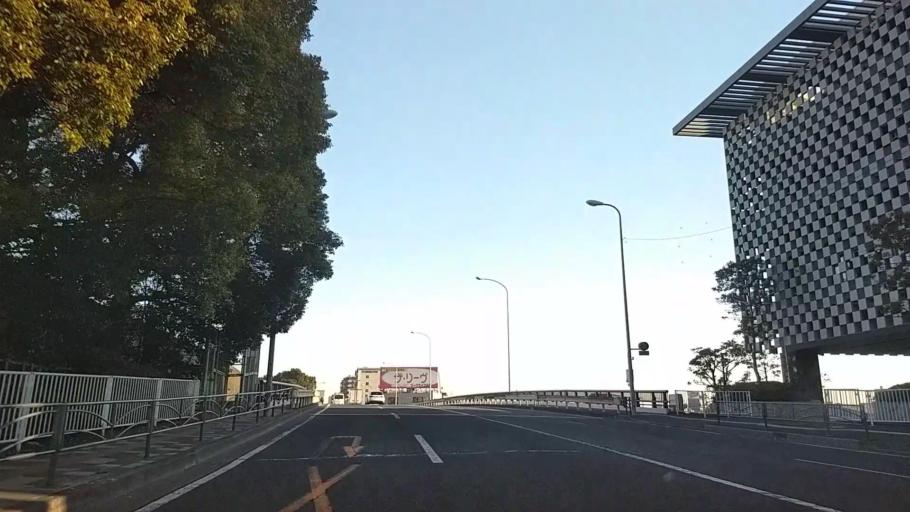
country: JP
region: Kanagawa
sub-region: Kawasaki-shi
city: Kawasaki
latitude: 35.5120
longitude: 139.6847
